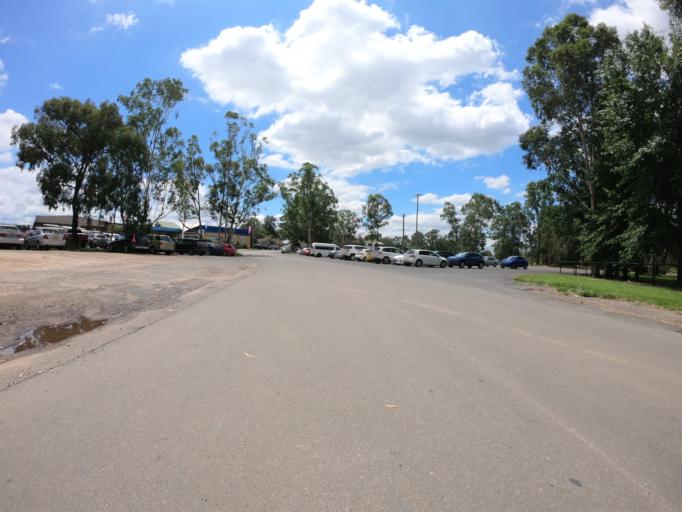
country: AU
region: New South Wales
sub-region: Penrith Municipality
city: Penrith
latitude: -33.7467
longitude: 150.6843
